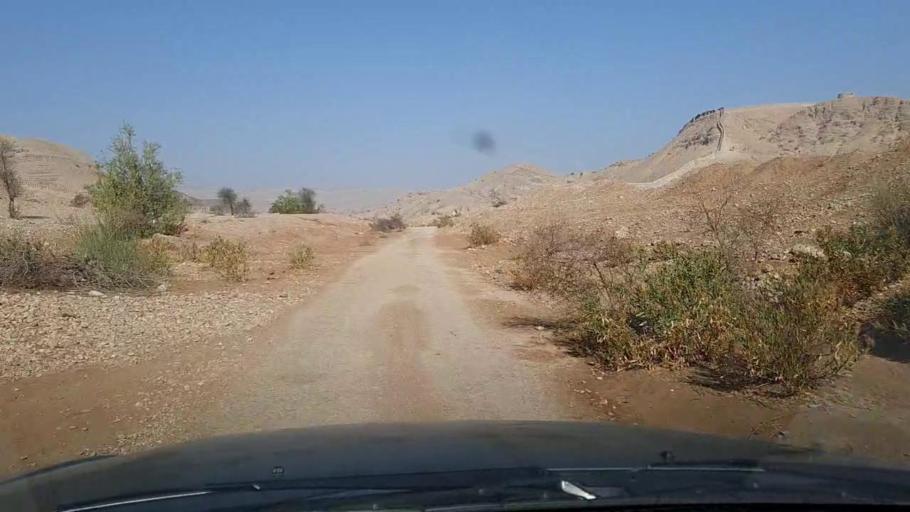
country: PK
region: Sindh
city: Sann
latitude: 25.8831
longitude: 67.9366
